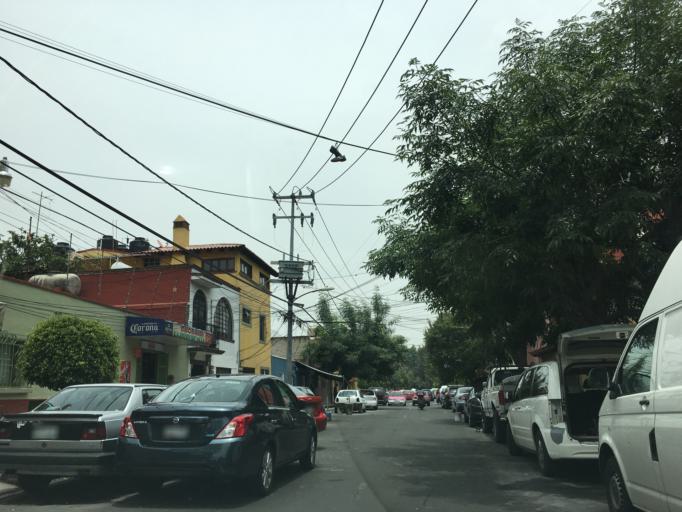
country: MX
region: Mexico City
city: Magdalena Contreras
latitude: 19.3423
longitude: -99.2018
